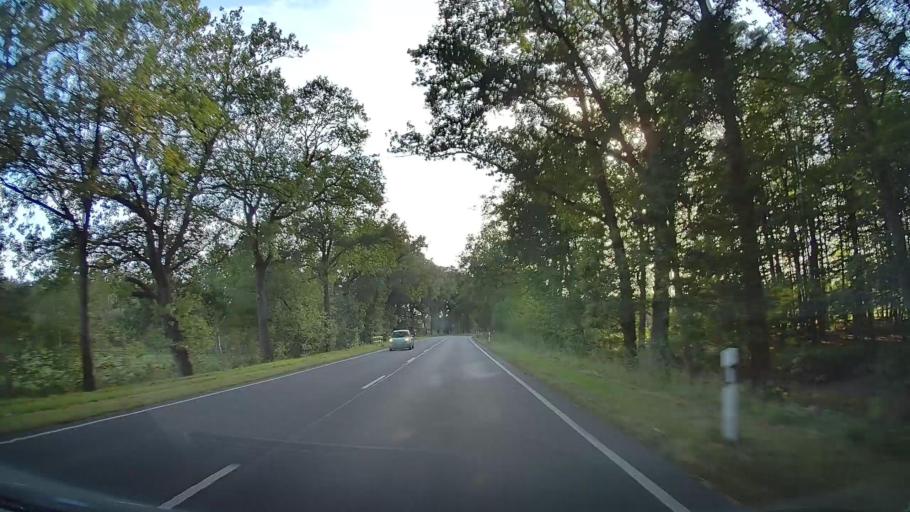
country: DE
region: Lower Saxony
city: Stemmen
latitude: 53.1963
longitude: 9.5256
